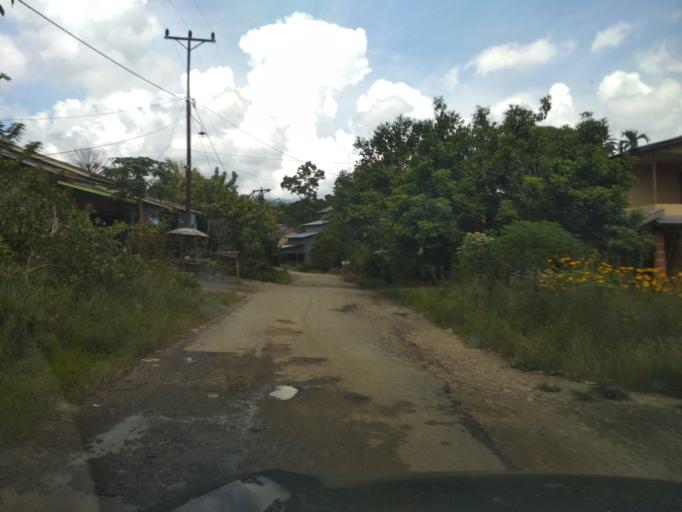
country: ID
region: West Kalimantan
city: Bengkayang
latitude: 0.7500
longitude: 110.1042
